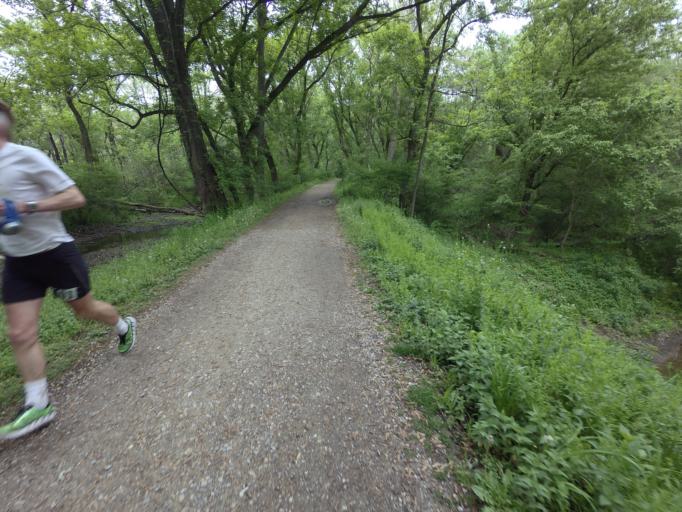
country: US
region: Maryland
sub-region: Frederick County
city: Brunswick
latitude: 39.3285
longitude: -77.6833
